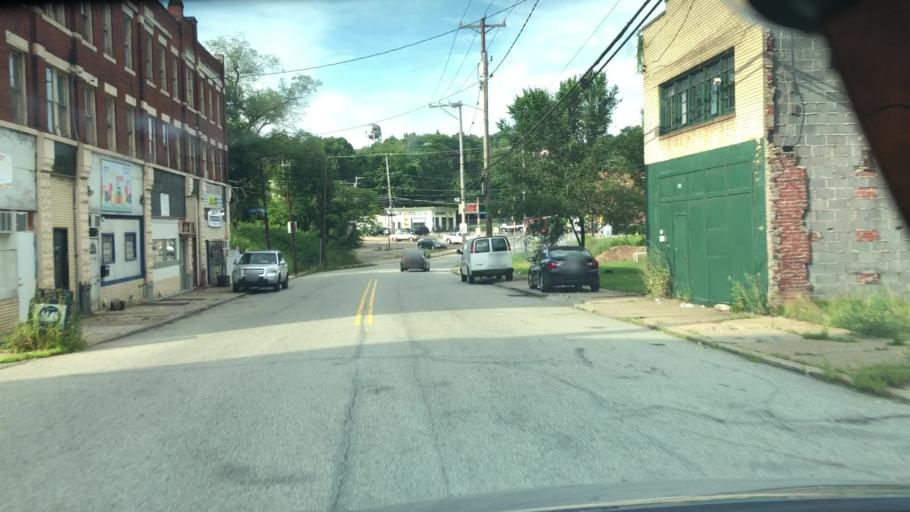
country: US
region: Pennsylvania
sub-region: Allegheny County
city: Aspinwall
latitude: 40.4678
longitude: -79.8969
